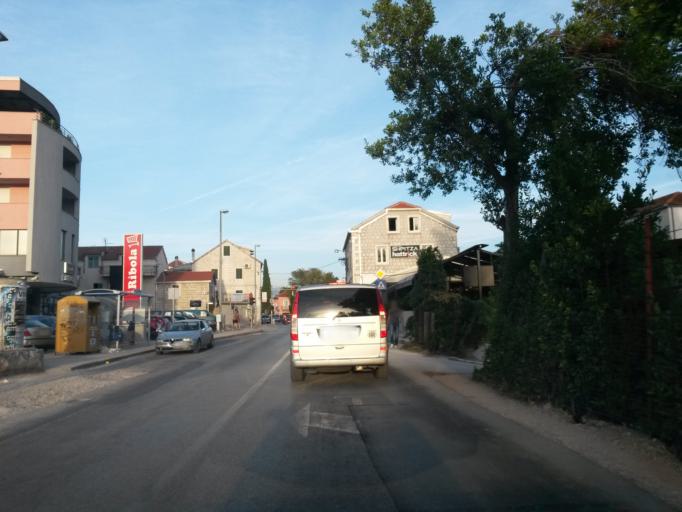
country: HR
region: Splitsko-Dalmatinska
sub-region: Grad Split
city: Split
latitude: 43.5501
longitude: 16.3846
